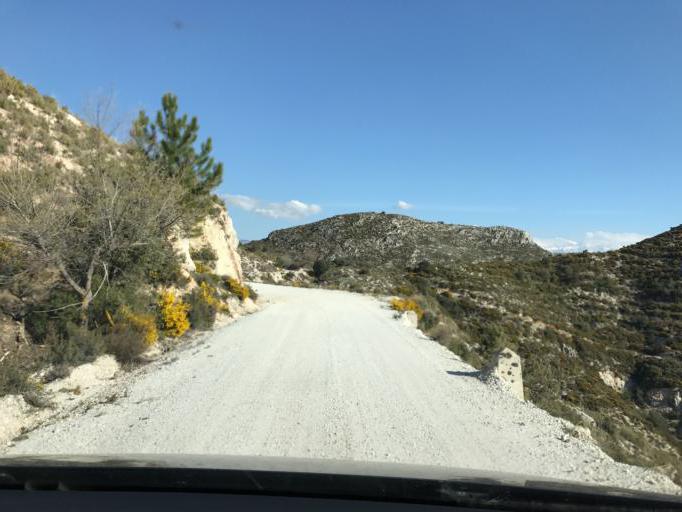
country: ES
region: Andalusia
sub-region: Provincia de Granada
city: Beas de Granada
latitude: 37.2436
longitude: -3.4560
